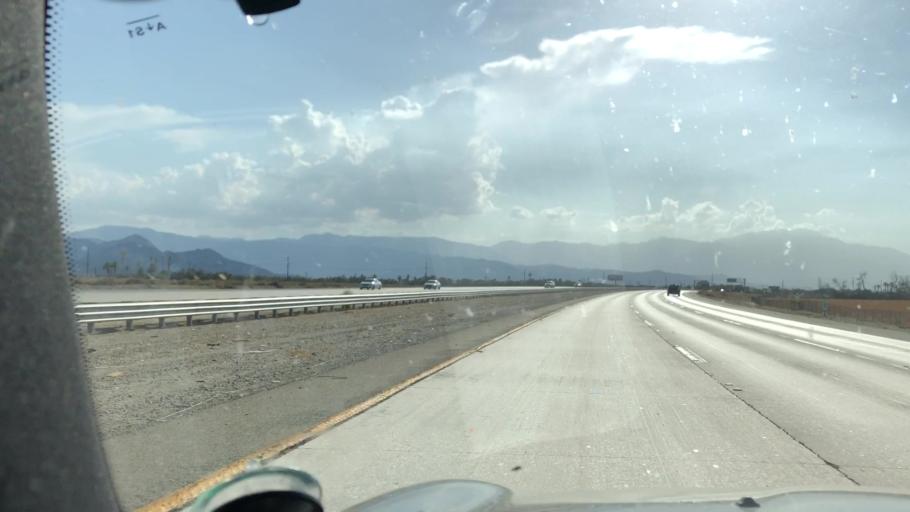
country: US
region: California
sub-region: Riverside County
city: Indio
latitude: 33.7384
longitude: -116.2431
